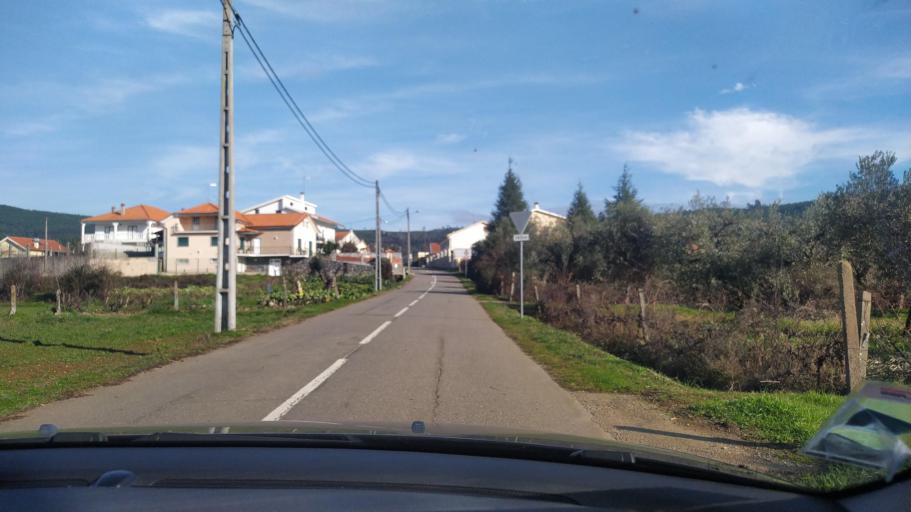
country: PT
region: Castelo Branco
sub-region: Concelho do Fundao
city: Aldeia de Joanes
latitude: 40.1883
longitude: -7.6395
